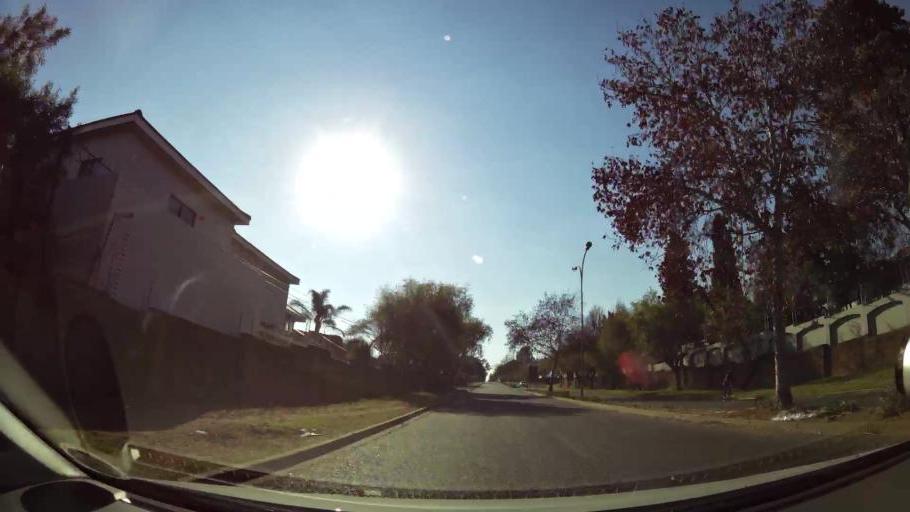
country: ZA
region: Gauteng
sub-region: City of Johannesburg Metropolitan Municipality
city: Modderfontein
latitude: -26.1451
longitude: 28.1434
